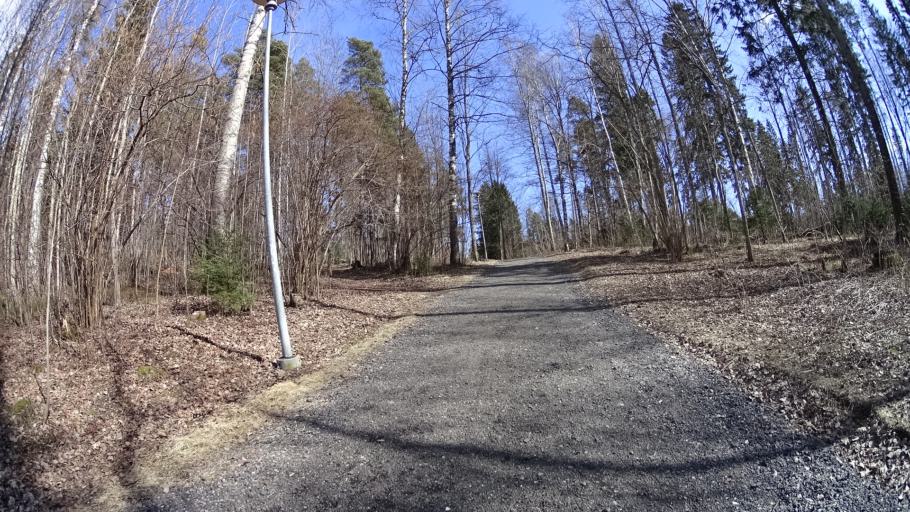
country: FI
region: Uusimaa
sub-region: Helsinki
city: Kilo
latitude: 60.2218
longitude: 24.7761
